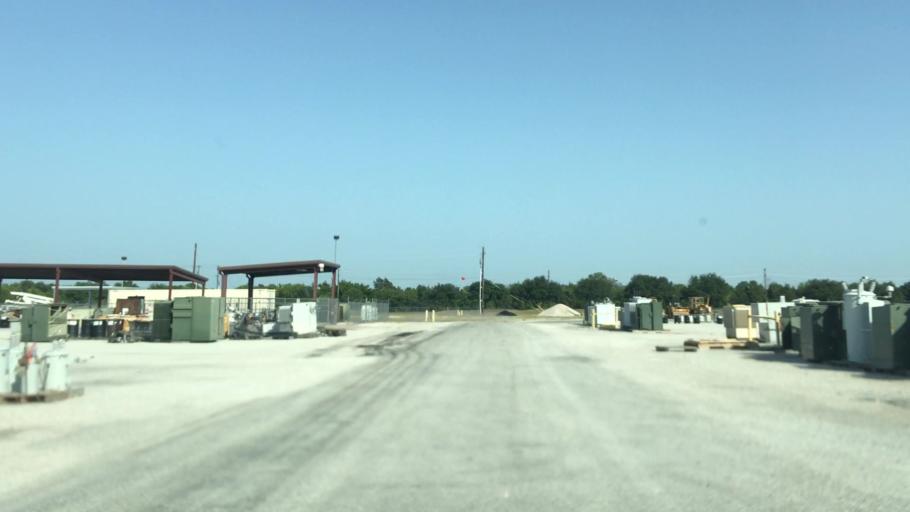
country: US
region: Texas
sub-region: Dallas County
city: Lancaster
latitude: 32.5656
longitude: -96.7692
